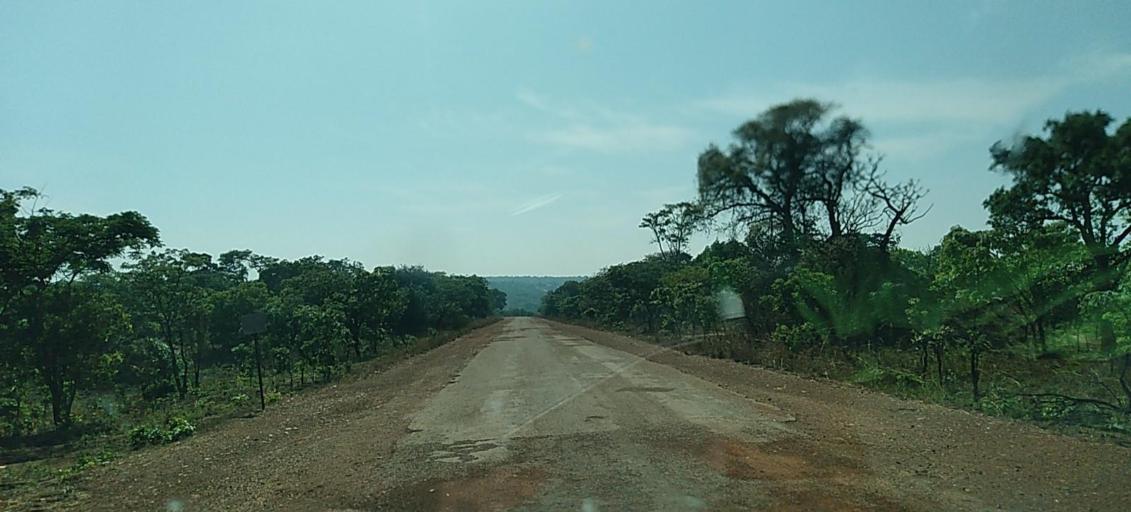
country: ZM
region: North-Western
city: Mwinilunga
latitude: -11.8230
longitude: 25.1151
